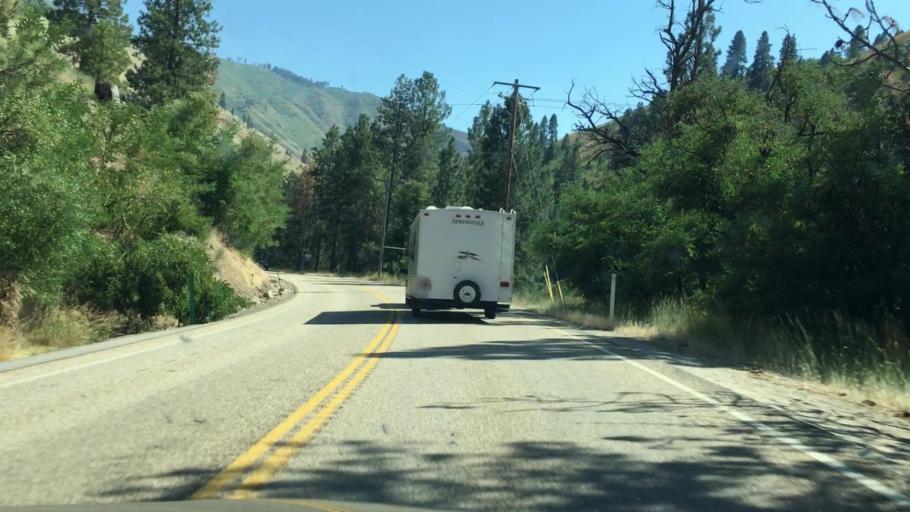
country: US
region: Idaho
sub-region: Boise County
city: Idaho City
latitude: 44.0510
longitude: -116.1329
